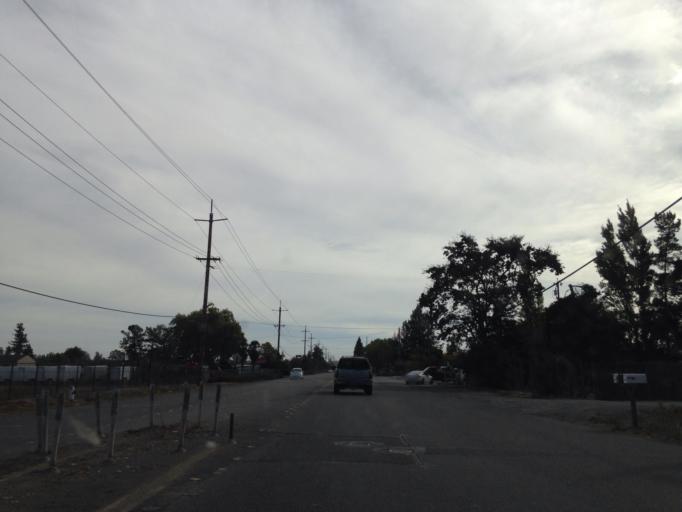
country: US
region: California
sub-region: Sonoma County
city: Roseland
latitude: 38.3857
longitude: -122.7137
